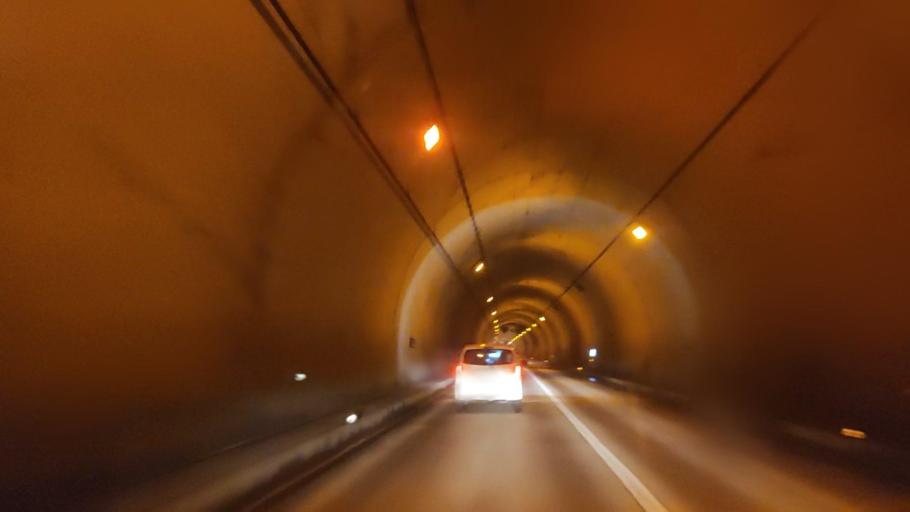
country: JP
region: Tottori
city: Kurayoshi
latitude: 35.3044
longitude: 133.7416
